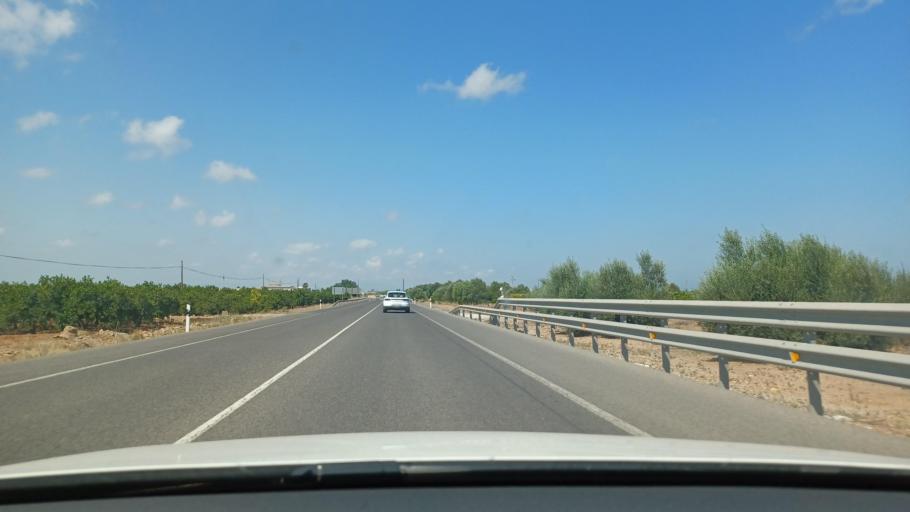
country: ES
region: Valencia
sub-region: Provincia de Castello
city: Moncofar
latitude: 39.8084
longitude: -0.1710
